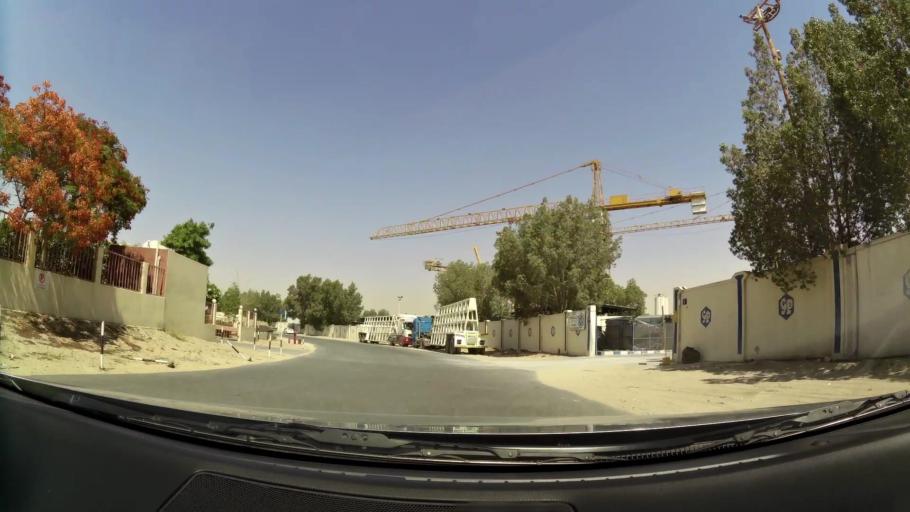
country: AE
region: Dubai
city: Dubai
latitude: 24.9817
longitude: 55.1523
